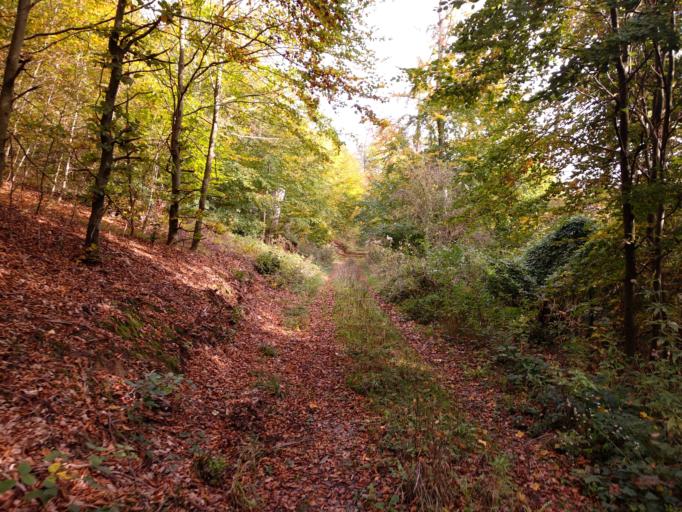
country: DE
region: North Rhine-Westphalia
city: Beverungen
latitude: 51.6854
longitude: 9.3722
